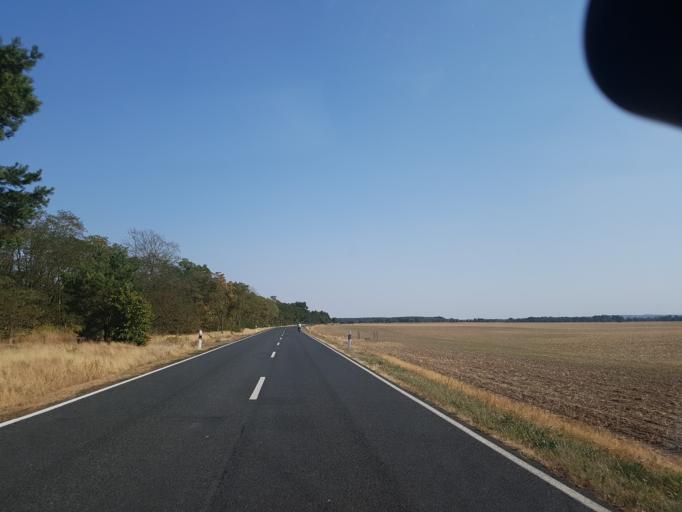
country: DE
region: Saxony
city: Beilrode
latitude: 51.5608
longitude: 13.0769
